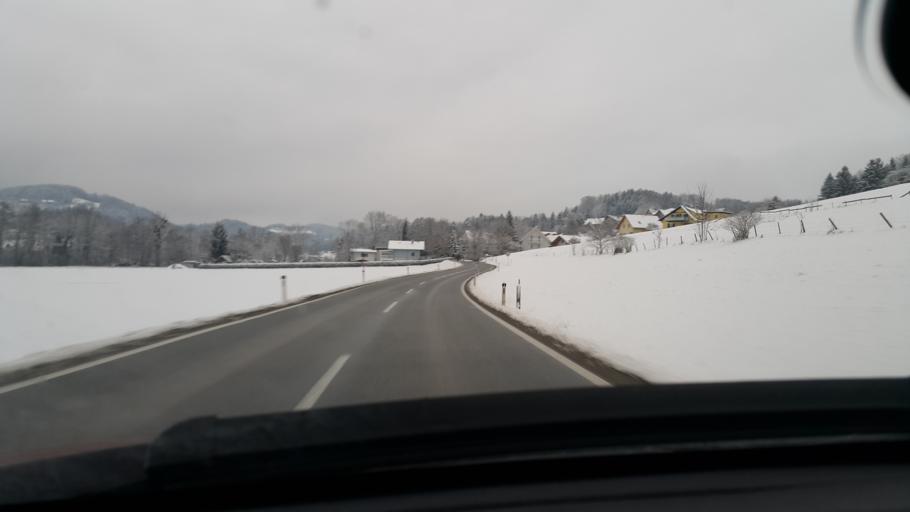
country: AT
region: Styria
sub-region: Politischer Bezirk Graz-Umgebung
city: Sankt Oswald bei Plankenwarth
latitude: 47.0698
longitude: 15.2697
